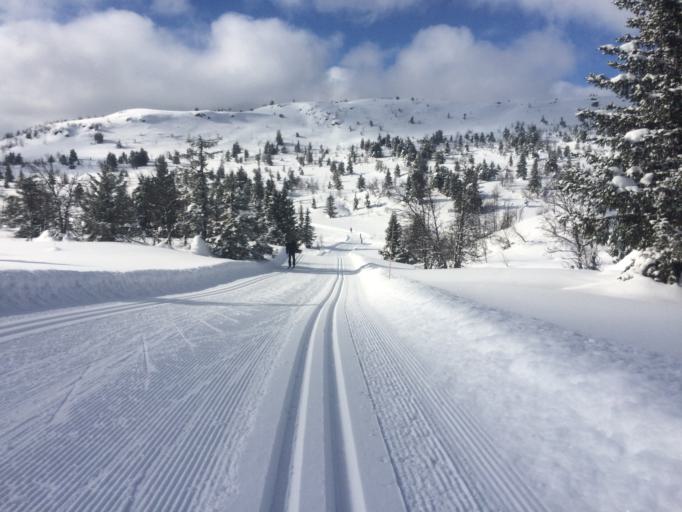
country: NO
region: Oppland
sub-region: Ringebu
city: Ringebu
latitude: 61.3561
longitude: 10.0575
